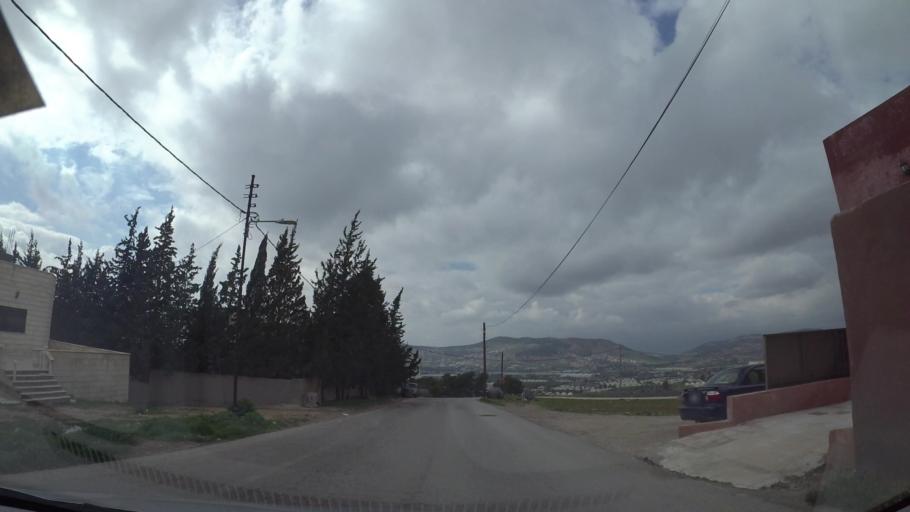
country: JO
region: Amman
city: Al Jubayhah
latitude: 32.0756
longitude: 35.8665
